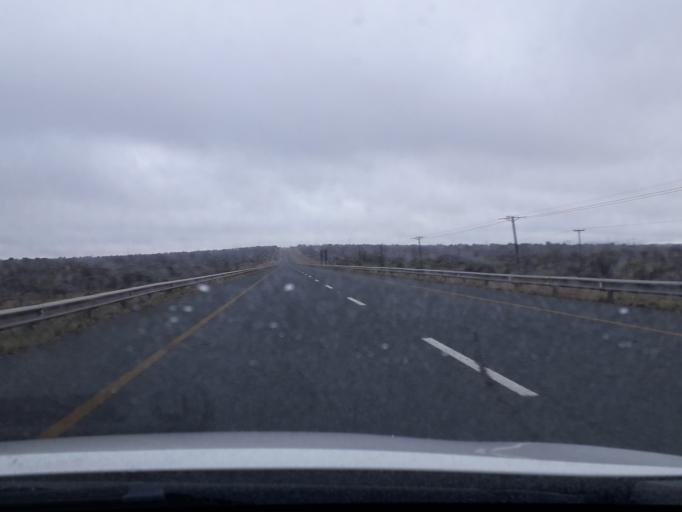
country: ZA
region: Limpopo
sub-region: Vhembe District Municipality
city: Louis Trichardt
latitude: -23.3956
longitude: 29.7612
